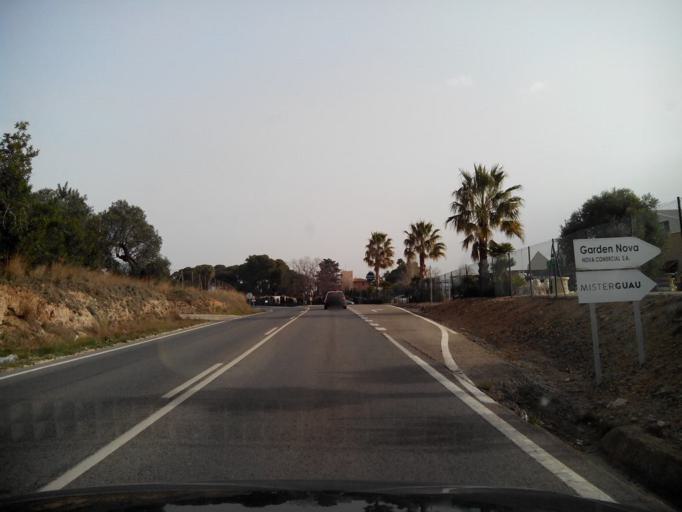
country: ES
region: Catalonia
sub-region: Provincia de Tarragona
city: Reus
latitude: 41.1127
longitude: 1.0924
